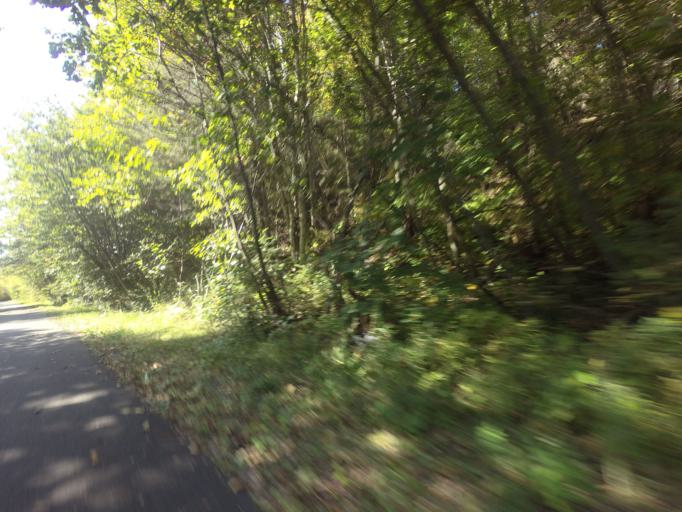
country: CA
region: Quebec
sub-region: Laurentides
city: Mont-Tremblant
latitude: 46.1127
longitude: -74.5105
